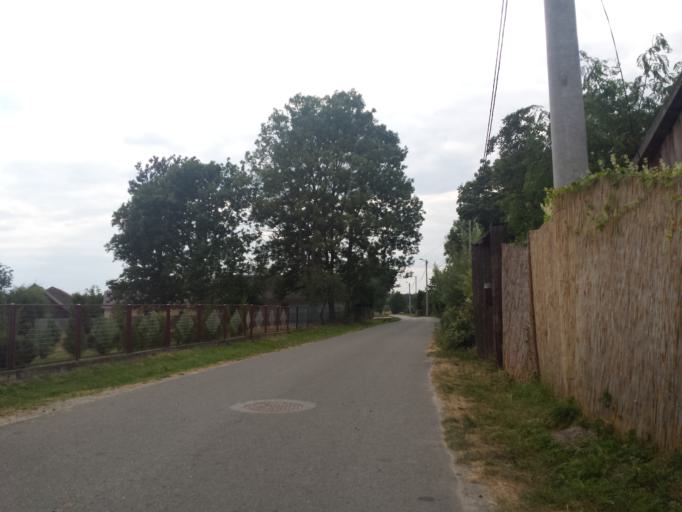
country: PL
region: Swietokrzyskie
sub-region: Powiat staszowski
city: Bogoria
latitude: 50.6615
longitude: 21.2332
